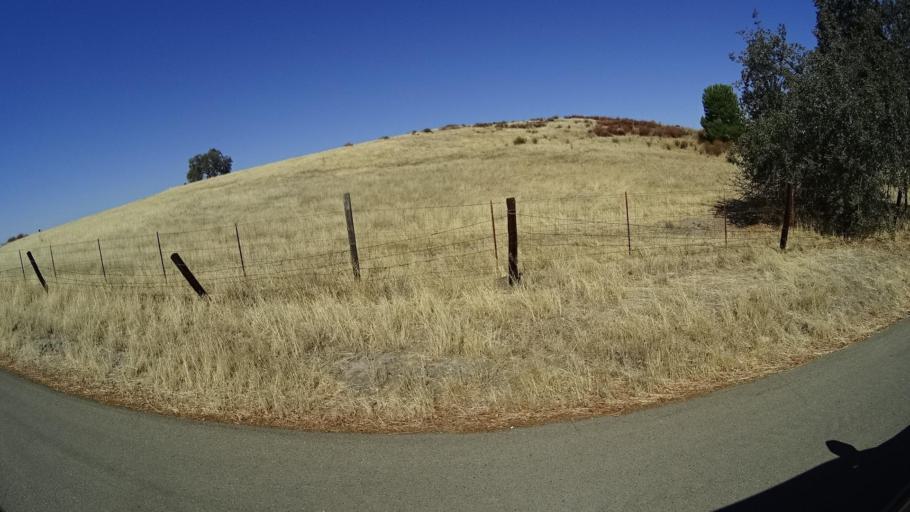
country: US
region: California
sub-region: San Luis Obispo County
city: Lake Nacimiento
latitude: 35.8083
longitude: -121.0438
